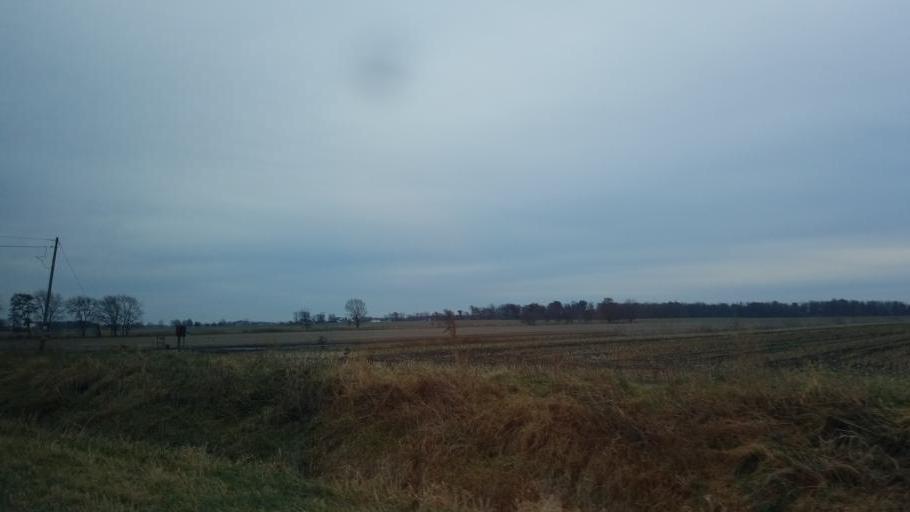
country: US
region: Indiana
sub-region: Adams County
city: Berne
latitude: 40.6736
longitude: -84.8699
